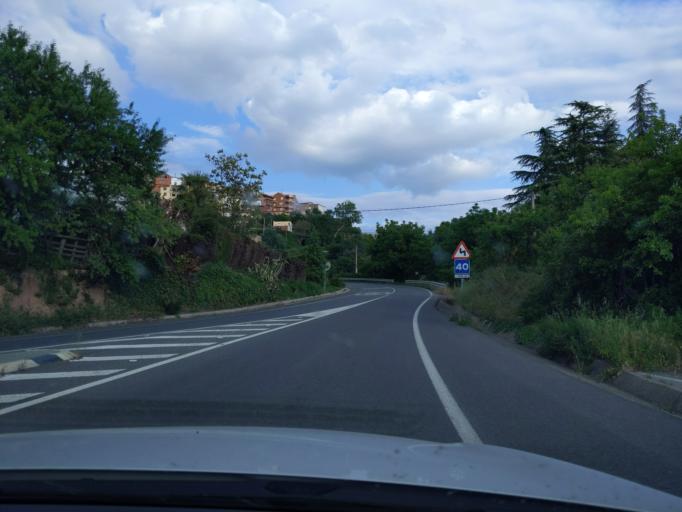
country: ES
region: La Rioja
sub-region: Provincia de La Rioja
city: Nalda
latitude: 42.3365
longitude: -2.4928
